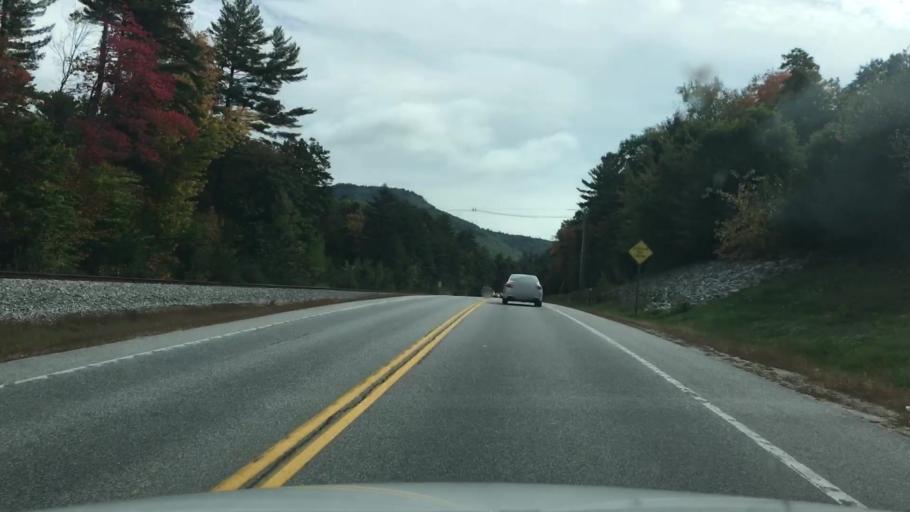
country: US
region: New Hampshire
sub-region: Carroll County
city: North Conway
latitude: 44.0434
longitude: -71.1208
